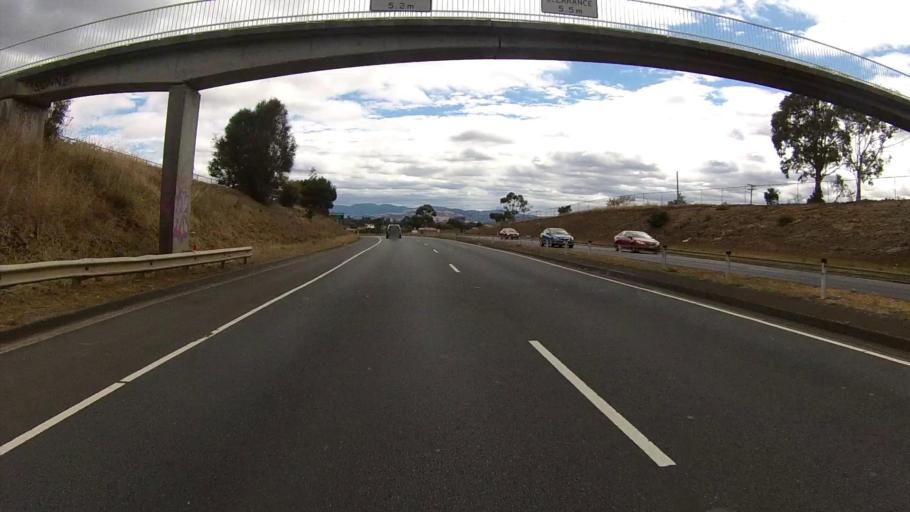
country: AU
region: Tasmania
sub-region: Glenorchy
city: Berriedale
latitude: -42.8049
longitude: 147.2493
